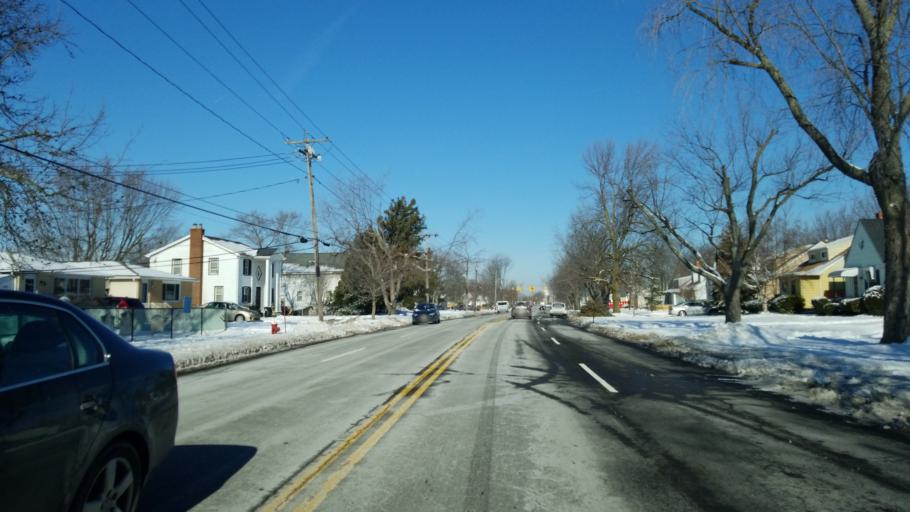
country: US
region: New York
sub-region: Erie County
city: Amherst
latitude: 42.9832
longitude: -78.8288
